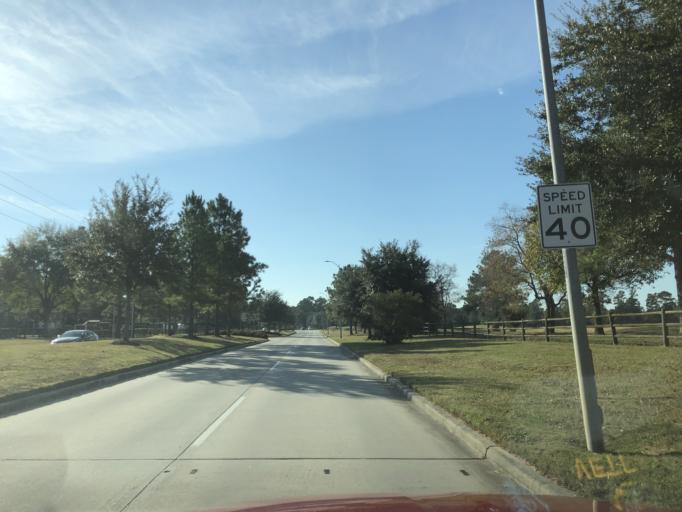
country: US
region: Texas
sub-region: Harris County
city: Tomball
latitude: 30.0429
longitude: -95.5629
